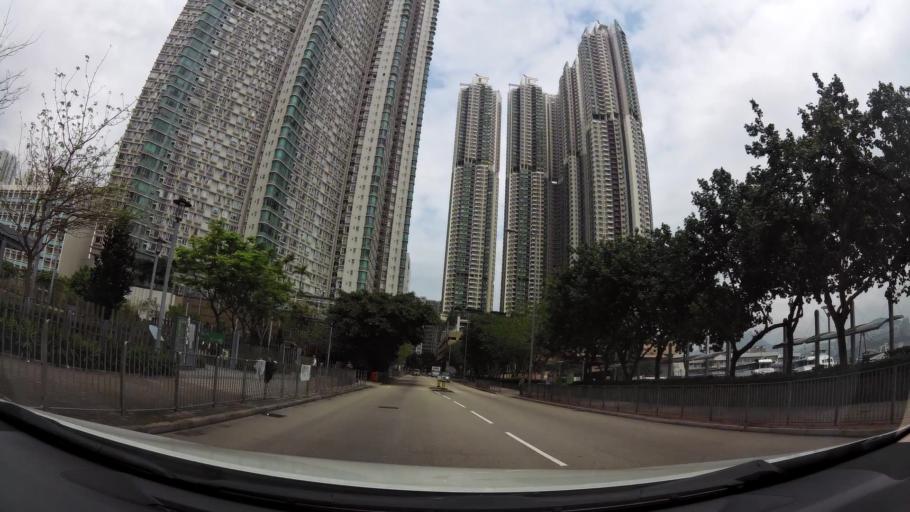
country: HK
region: Wanchai
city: Wan Chai
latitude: 22.2832
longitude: 114.2258
